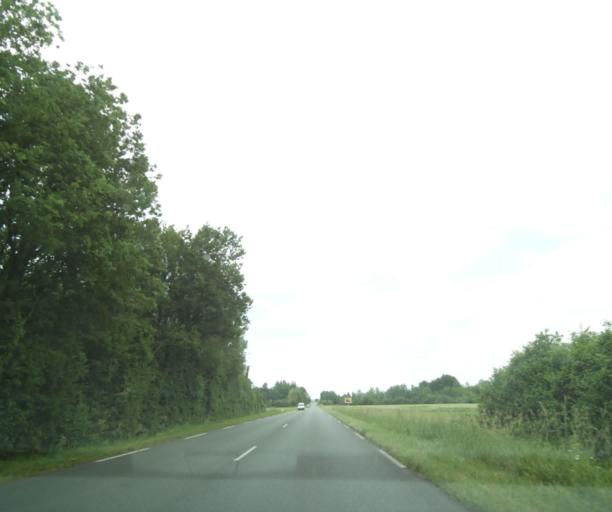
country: FR
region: Pays de la Loire
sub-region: Departement de Maine-et-Loire
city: Montreuil-Bellay
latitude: 47.1031
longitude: -0.1668
